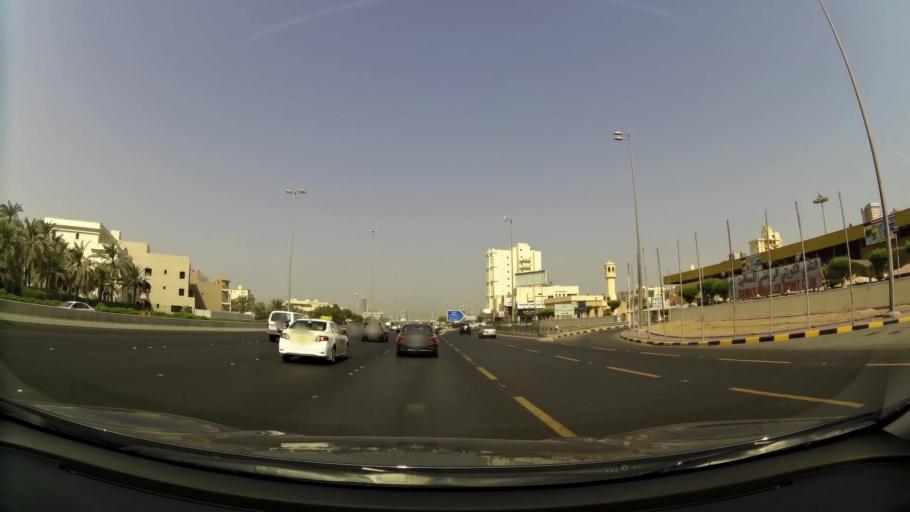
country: KW
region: Muhafazat Hawalli
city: Hawalli
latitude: 29.3362
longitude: 48.0036
